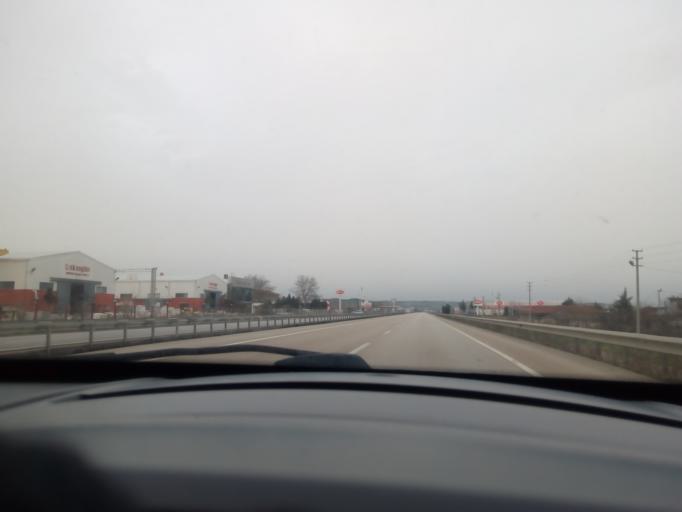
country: TR
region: Bursa
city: Tatkavakli
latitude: 40.0294
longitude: 28.3074
